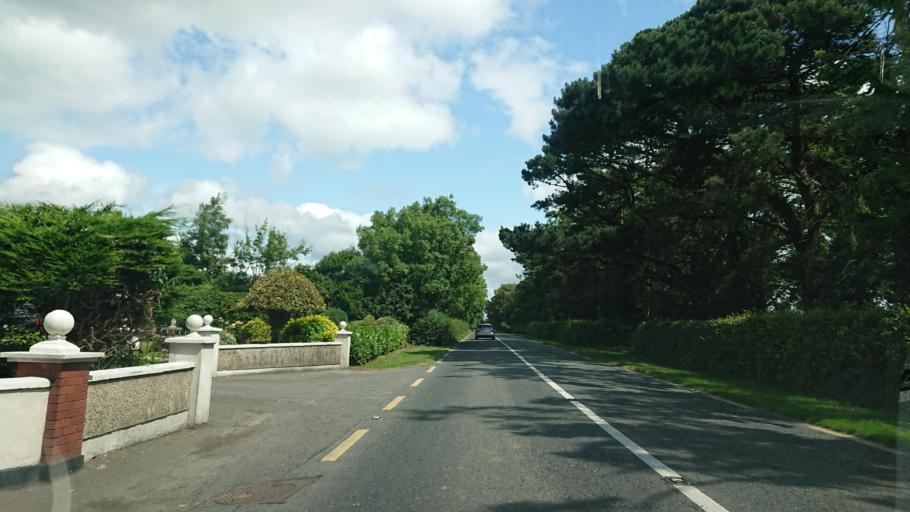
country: IE
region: Leinster
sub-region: Kildare
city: Kilcock
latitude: 53.3870
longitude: -6.7022
